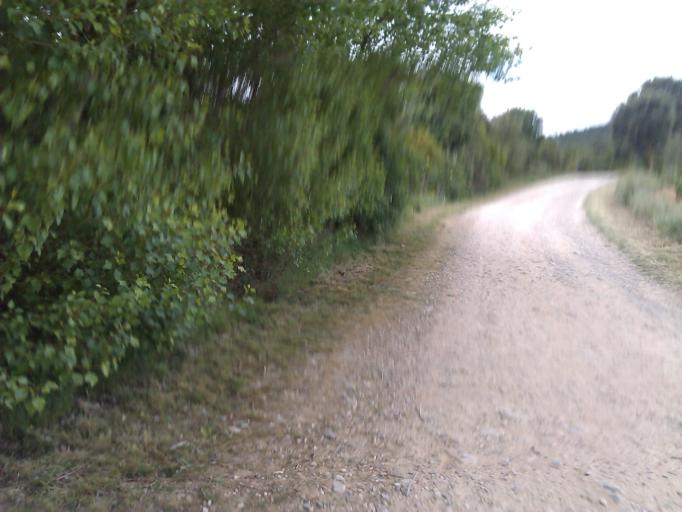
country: ES
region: La Rioja
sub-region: Provincia de La Rioja
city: Navarrete
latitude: 42.4388
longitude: -2.5206
